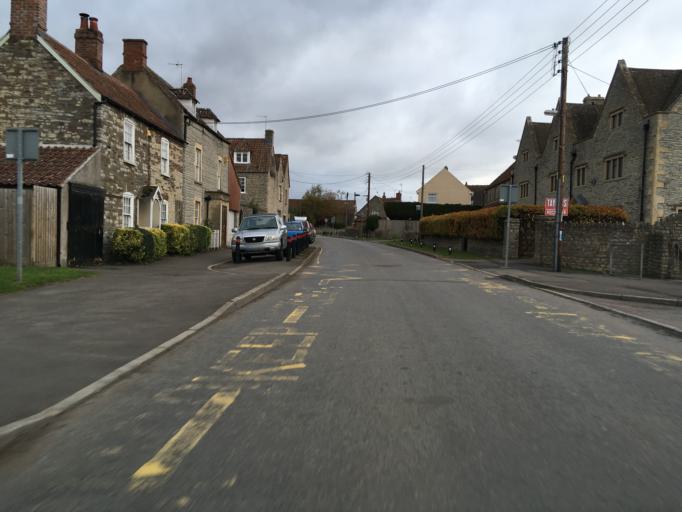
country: GB
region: England
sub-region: South Gloucestershire
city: Pucklechurch
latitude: 51.4883
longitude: -2.4322
